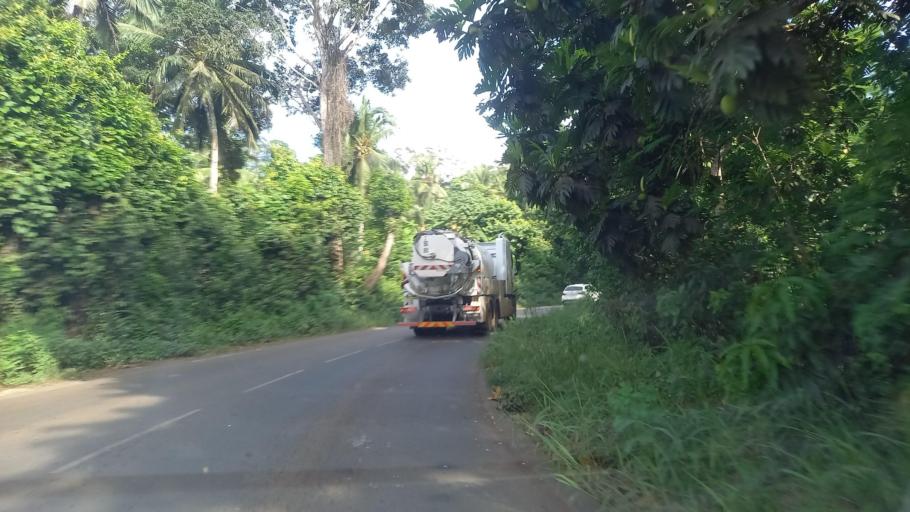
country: YT
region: Chiconi
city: Chiconi
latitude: -12.8071
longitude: 45.1256
